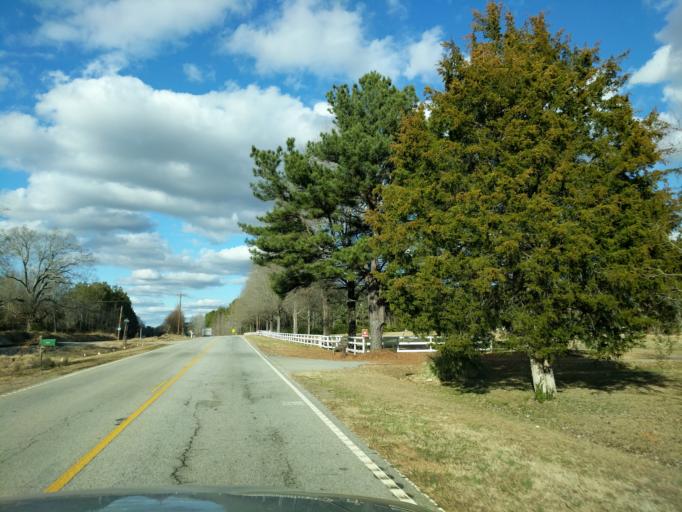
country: US
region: South Carolina
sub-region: Laurens County
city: Watts Mills
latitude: 34.5835
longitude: -81.9954
